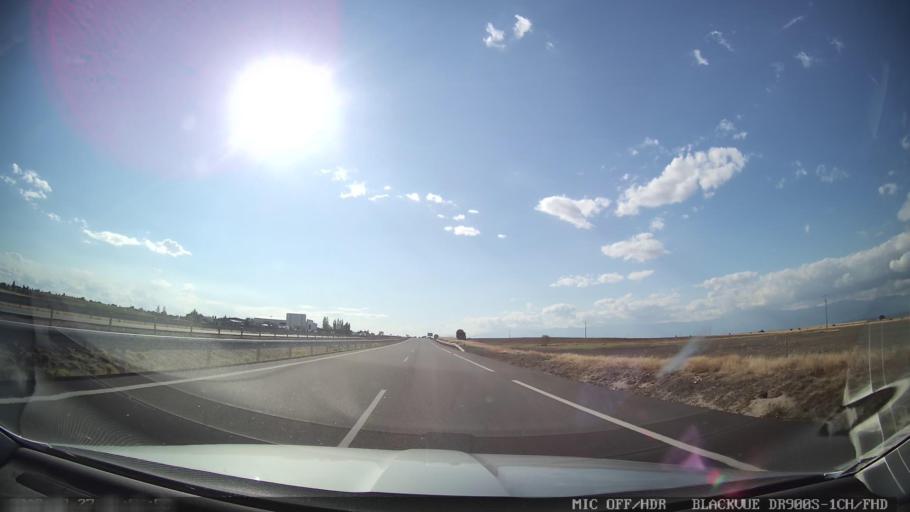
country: ES
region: Castille-La Mancha
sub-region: Province of Toledo
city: Torralba de Oropesa
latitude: 39.9276
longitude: -5.1312
